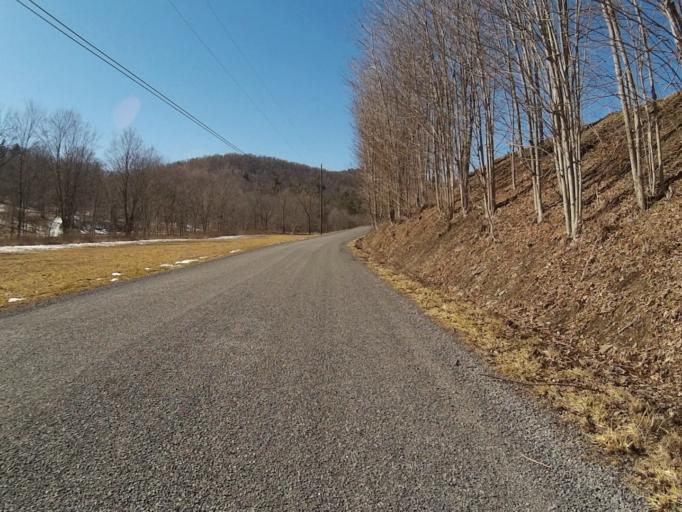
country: US
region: Pennsylvania
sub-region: Centre County
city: Stormstown
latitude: 40.8367
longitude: -78.0179
